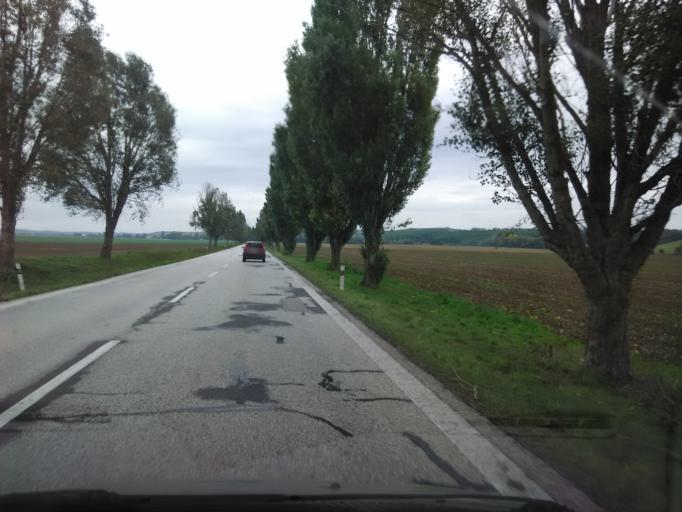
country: SK
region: Nitriansky
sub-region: Okres Nitra
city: Vrable
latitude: 48.2357
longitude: 18.3386
